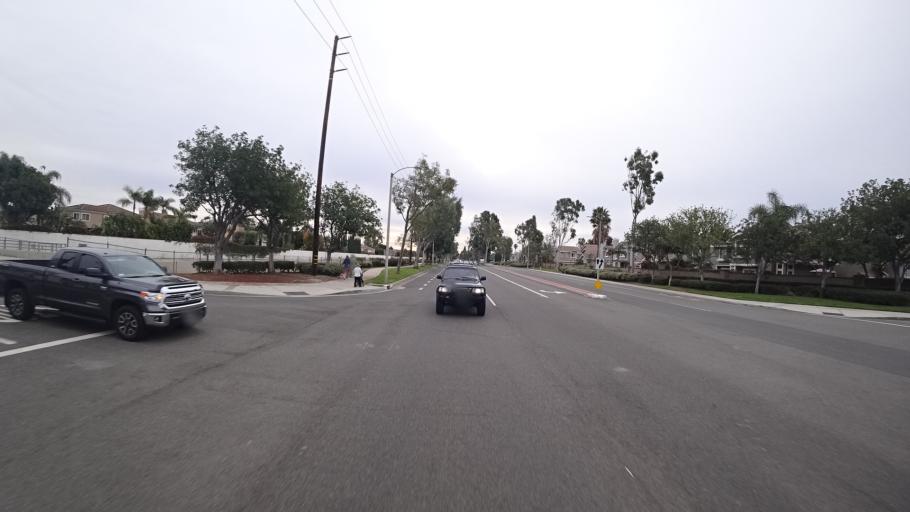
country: US
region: California
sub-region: Orange County
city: Tustin
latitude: 33.7327
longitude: -117.8007
